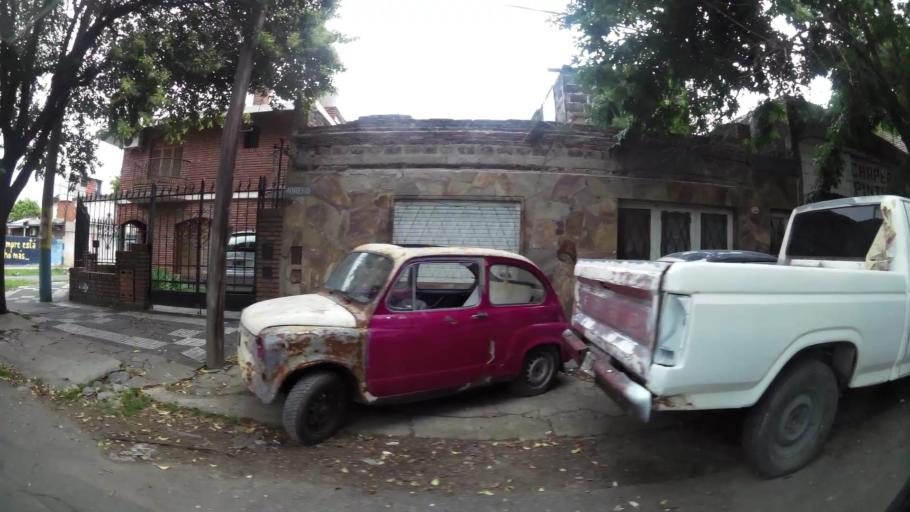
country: AR
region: Santa Fe
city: Gobernador Galvez
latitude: -32.9980
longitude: -60.6622
